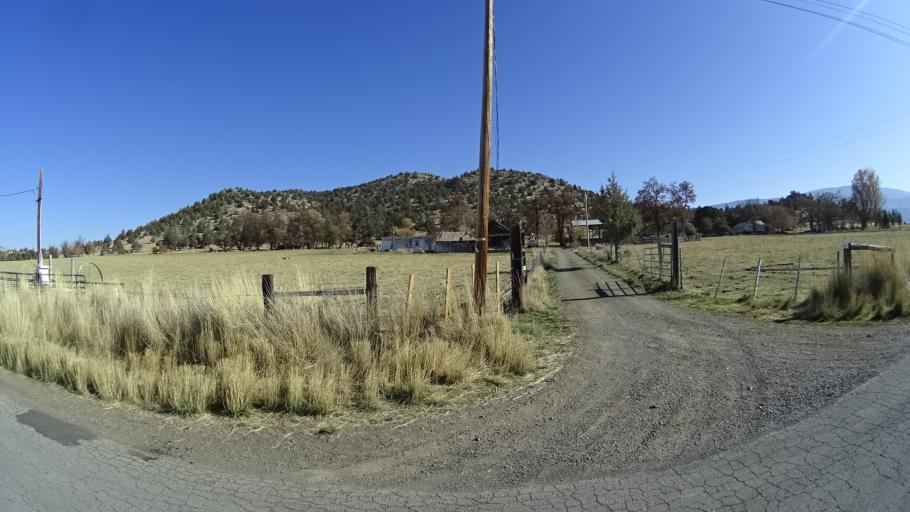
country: US
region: California
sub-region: Siskiyou County
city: Montague
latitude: 41.7048
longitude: -122.3790
